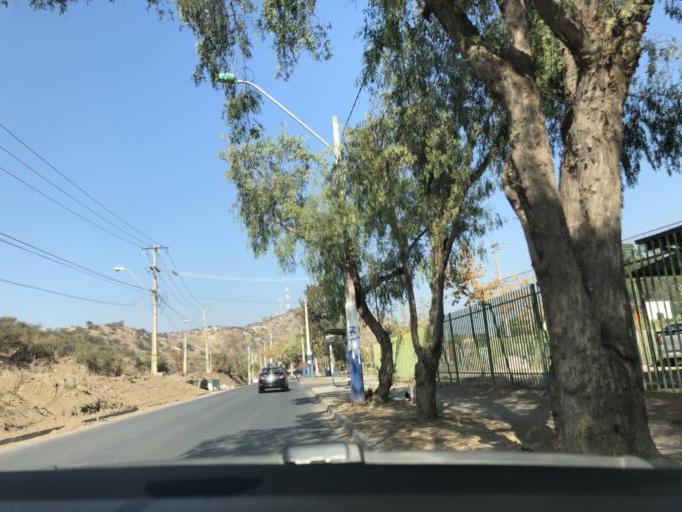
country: CL
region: Santiago Metropolitan
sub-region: Provincia de Cordillera
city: Puente Alto
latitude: -33.6188
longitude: -70.6033
